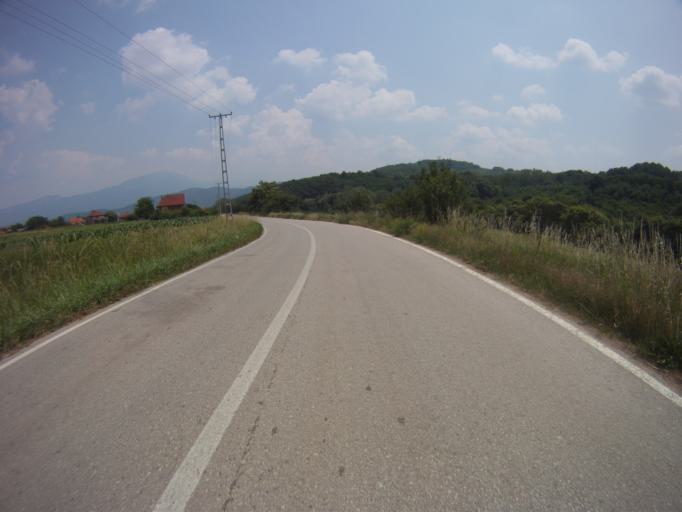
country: RS
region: Central Serbia
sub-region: Nisavski Okrug
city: Gadzin Han
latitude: 43.2053
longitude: 21.9910
